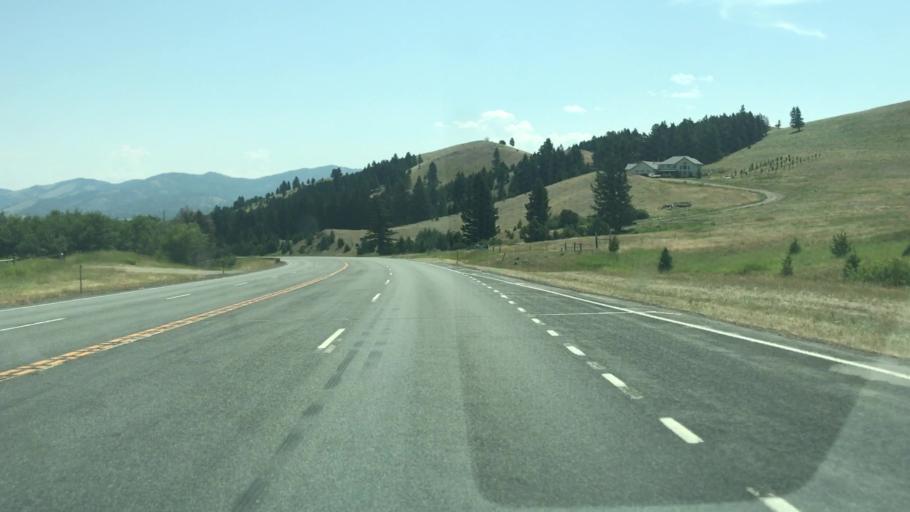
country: US
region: Montana
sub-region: Lewis and Clark County
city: Helena West Side
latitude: 46.5732
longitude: -112.2358
